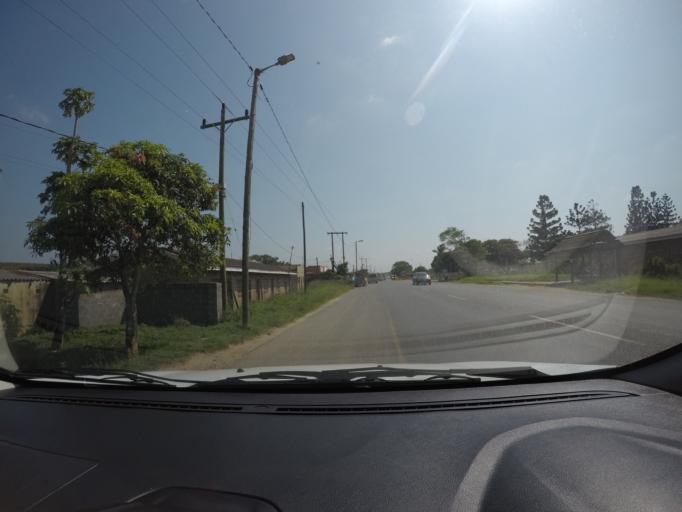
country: ZA
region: KwaZulu-Natal
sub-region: uThungulu District Municipality
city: eSikhawini
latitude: -28.8764
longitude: 31.8947
